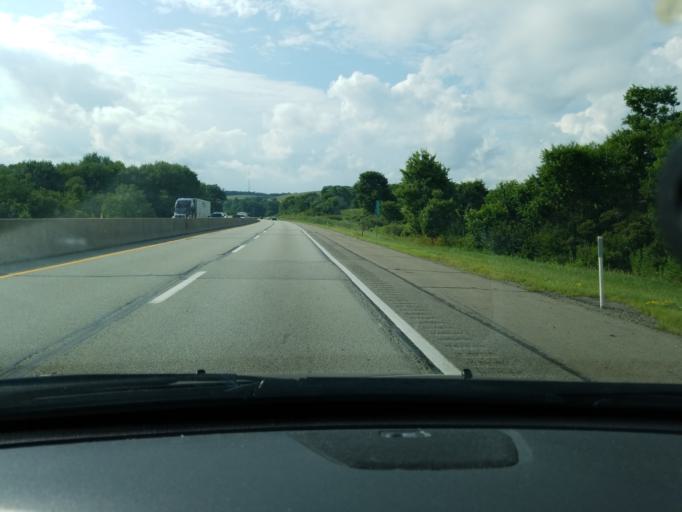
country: US
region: Pennsylvania
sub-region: Butler County
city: Fernway
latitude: 40.7293
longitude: -80.1619
